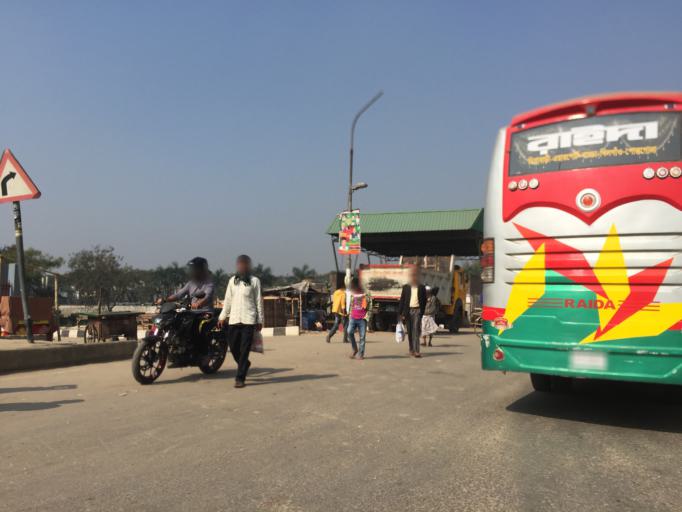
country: BD
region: Dhaka
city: Tungi
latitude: 23.8208
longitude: 90.4197
